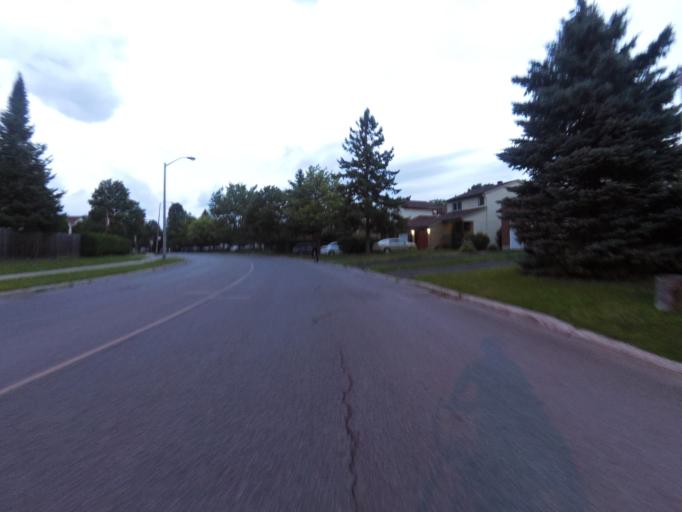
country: CA
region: Quebec
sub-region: Outaouais
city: Gatineau
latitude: 45.4623
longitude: -75.4925
